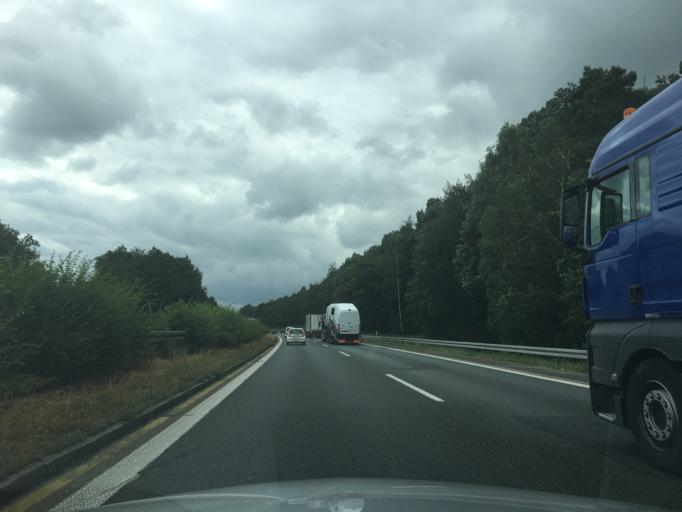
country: DE
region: Bavaria
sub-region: Regierungsbezirk Mittelfranken
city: Wachenroth
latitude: 49.7313
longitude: 10.6728
